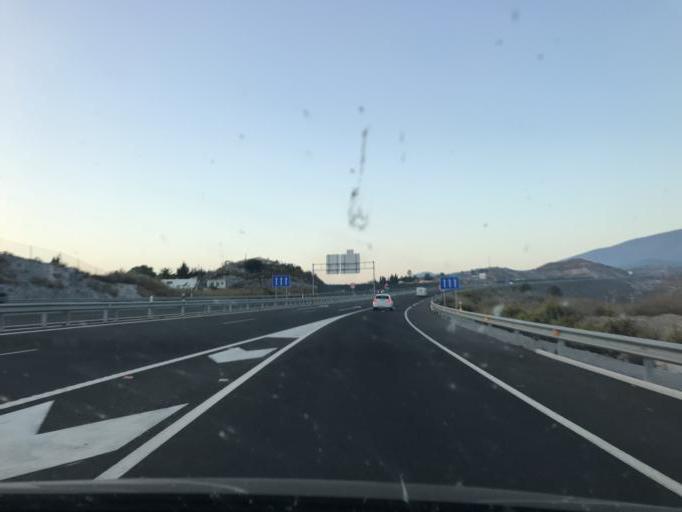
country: ES
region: Andalusia
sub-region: Provincia de Granada
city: Motril
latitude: 36.7420
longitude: -3.4869
